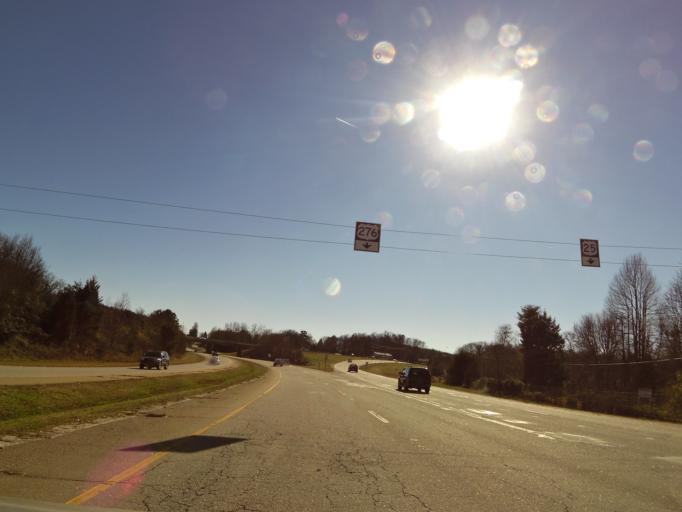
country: US
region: South Carolina
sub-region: Greenville County
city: Travelers Rest
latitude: 34.9498
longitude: -82.4393
